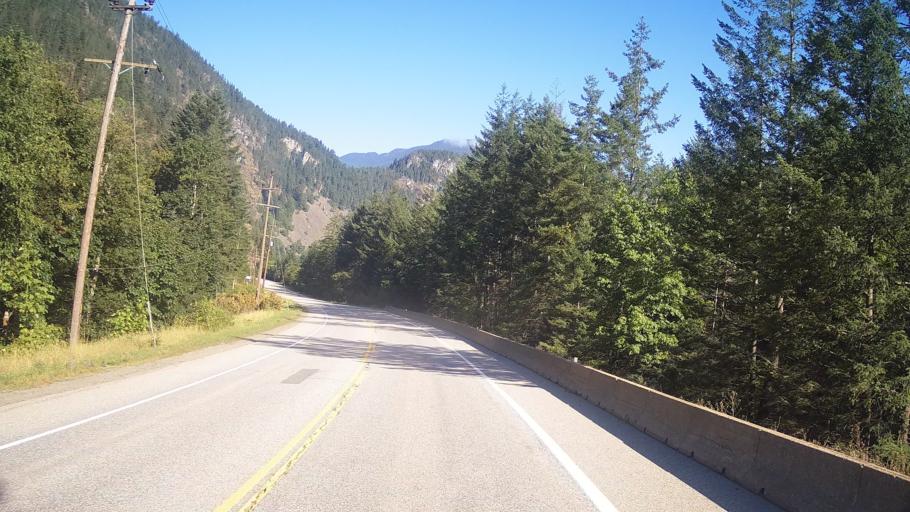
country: CA
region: British Columbia
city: Hope
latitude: 49.6324
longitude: -121.3945
